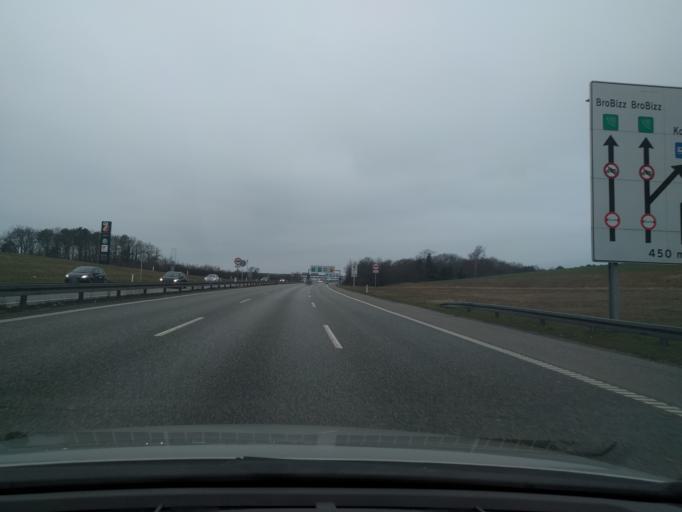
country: DK
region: Zealand
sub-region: Slagelse Kommune
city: Korsor
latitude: 55.3472
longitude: 11.1168
